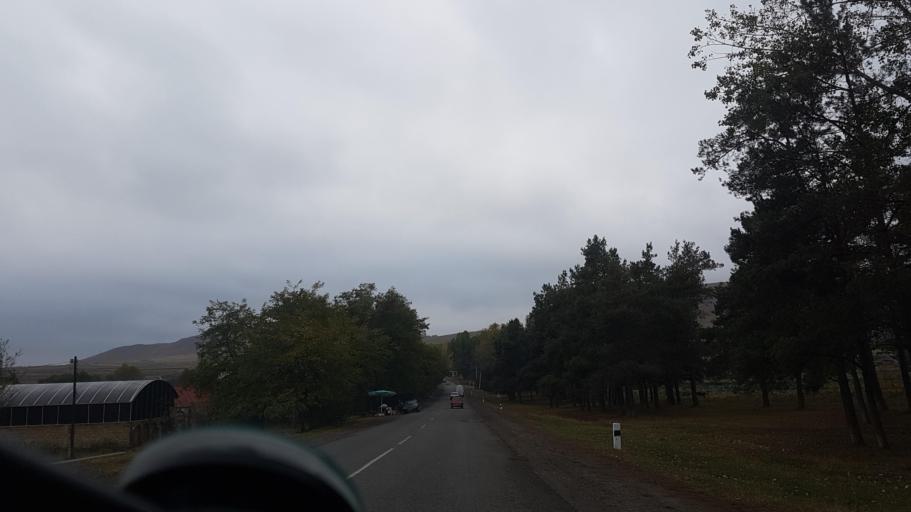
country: AZ
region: Gadabay Rayon
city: Ariqdam
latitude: 40.6375
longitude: 45.8130
